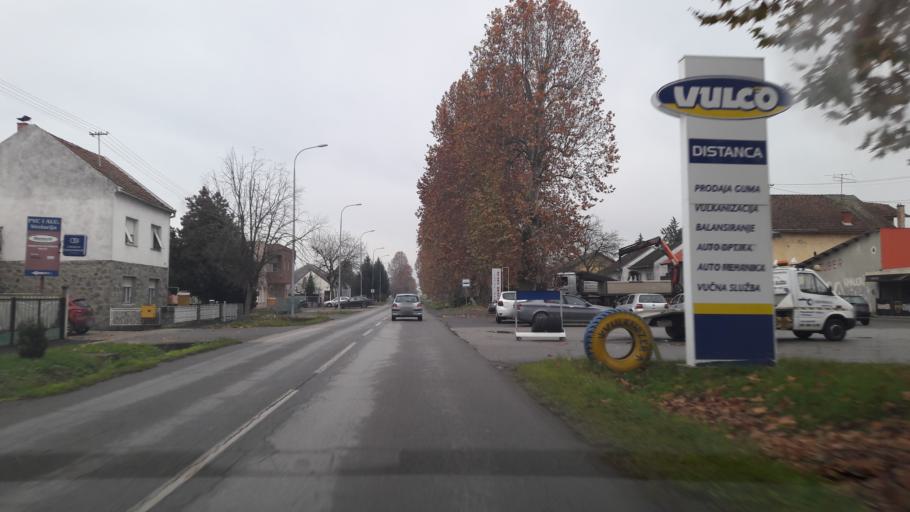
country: HR
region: Osjecko-Baranjska
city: Visnjevac
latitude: 45.5721
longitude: 18.6051
